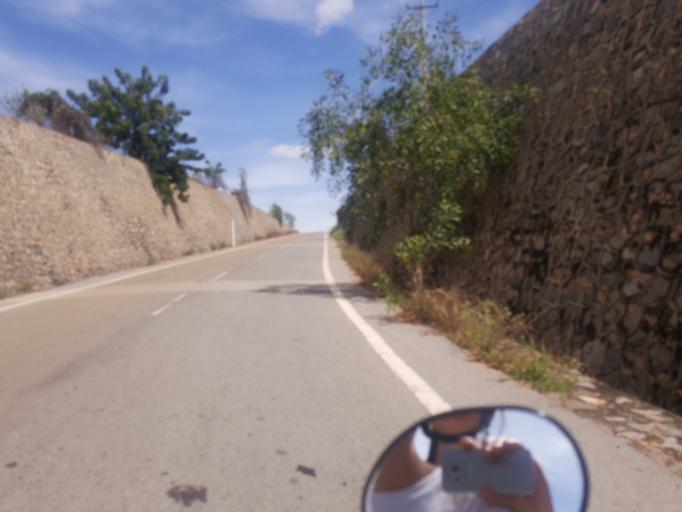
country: VN
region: Binh Thuan
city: Phan Thiet
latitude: 10.9589
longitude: 108.2144
